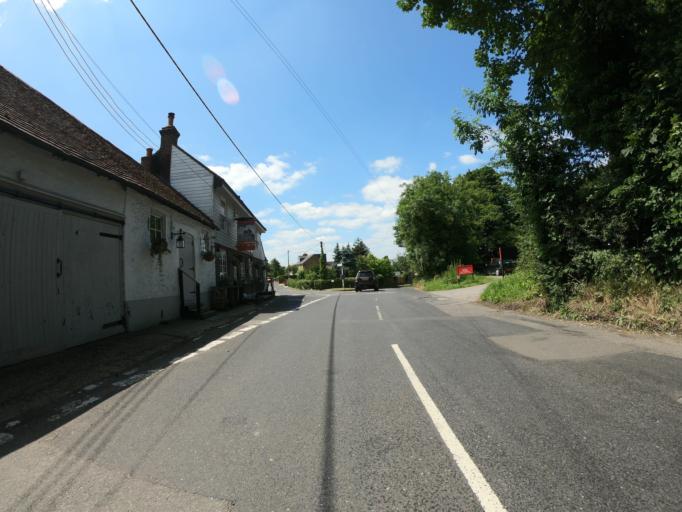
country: GB
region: England
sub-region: Kent
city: Halstead
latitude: 51.3162
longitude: 0.1286
